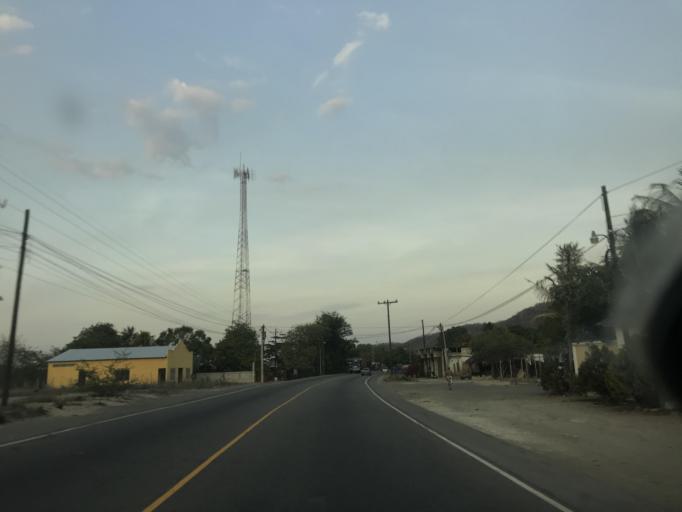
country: GT
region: Zacapa
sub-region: Municipio de Zacapa
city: Gualan
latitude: 15.0868
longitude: -89.4652
